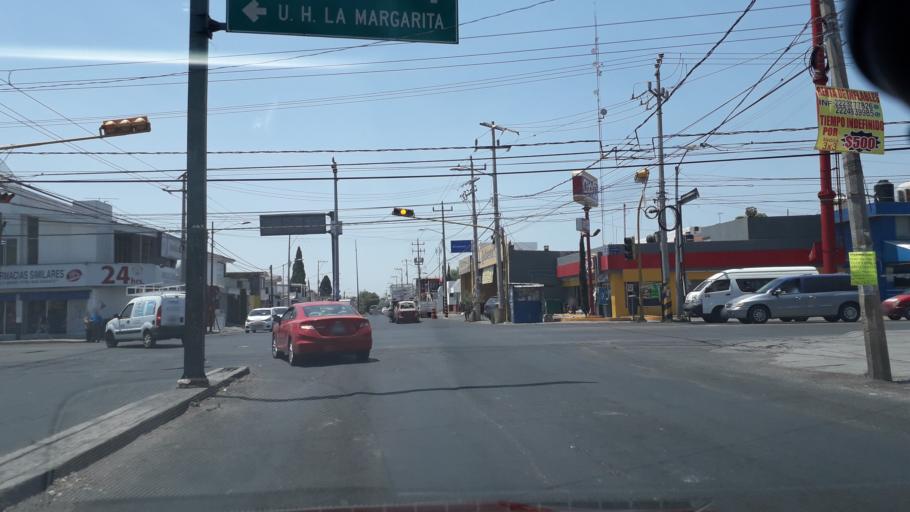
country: MX
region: Puebla
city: Puebla
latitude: 19.0138
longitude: -98.1930
